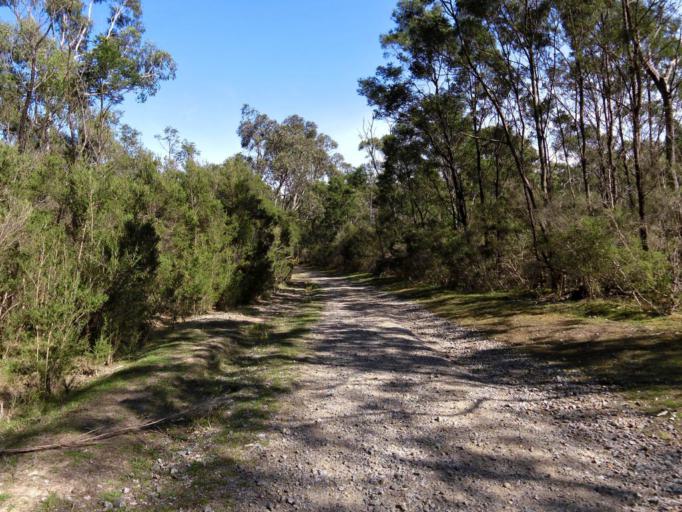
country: AU
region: Victoria
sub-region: Yarra Ranges
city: Lysterfield
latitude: -37.9402
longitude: 145.2895
